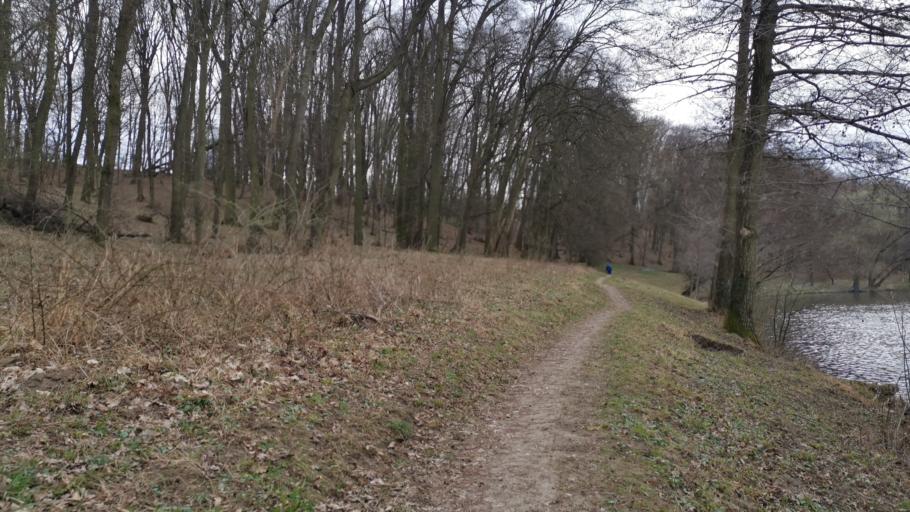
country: CZ
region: South Moravian
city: Petrov
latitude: 48.8426
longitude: 17.3115
